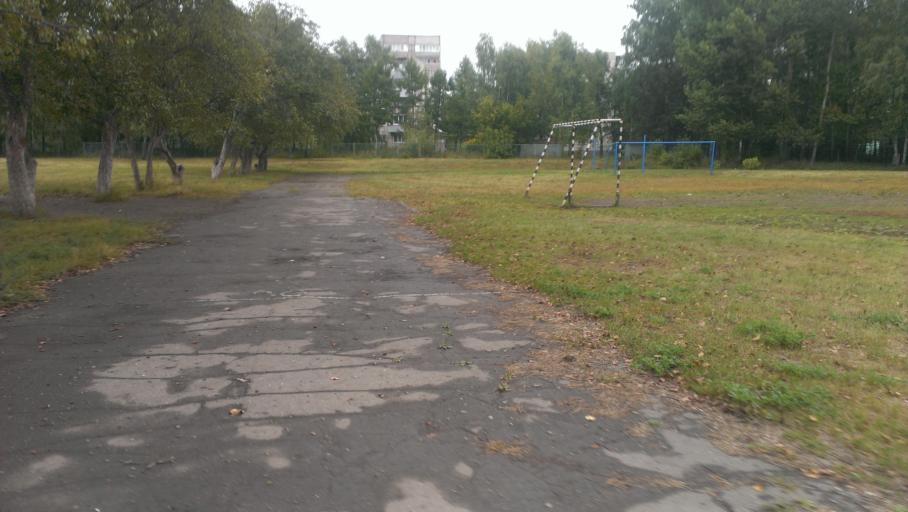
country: RU
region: Altai Krai
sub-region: Gorod Barnaulskiy
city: Barnaul
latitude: 53.3685
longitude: 83.6826
